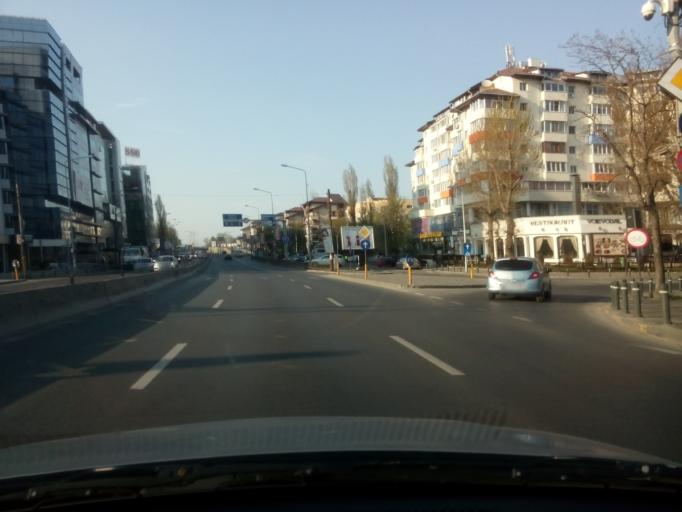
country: RO
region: Ilfov
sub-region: Comuna Otopeni
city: Otopeni
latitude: 44.4899
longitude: 26.0790
